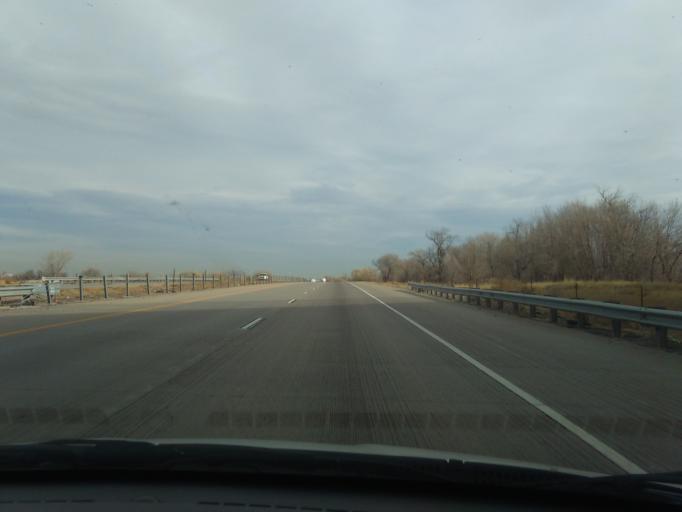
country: US
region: Colorado
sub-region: Adams County
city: Brighton
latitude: 39.9156
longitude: -104.8148
